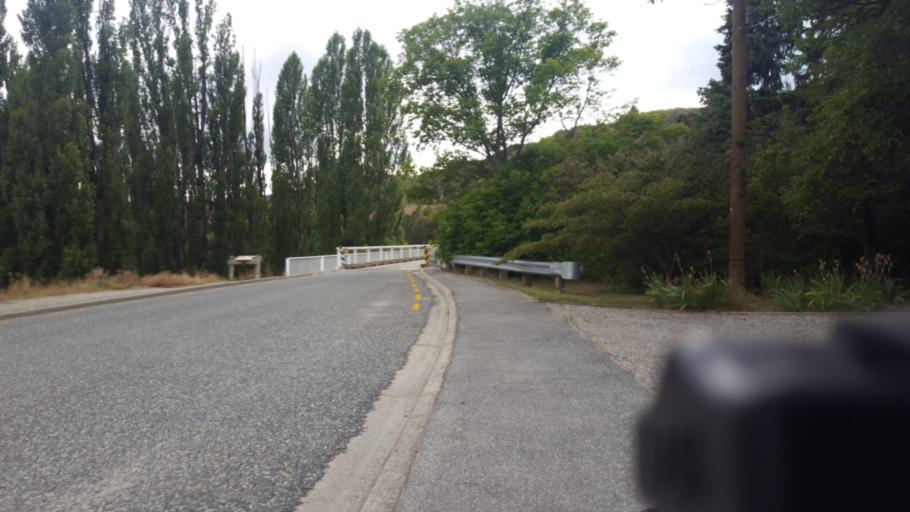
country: NZ
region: Otago
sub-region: Queenstown-Lakes District
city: Wanaka
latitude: -45.2501
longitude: 169.4009
